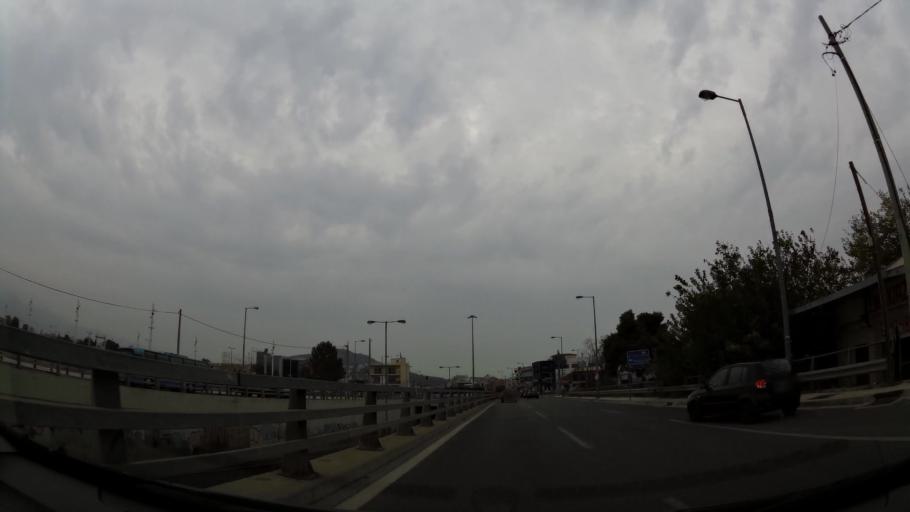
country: GR
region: Attica
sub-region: Nomarchia Athinas
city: Irakleio
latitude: 38.0413
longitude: 23.7772
